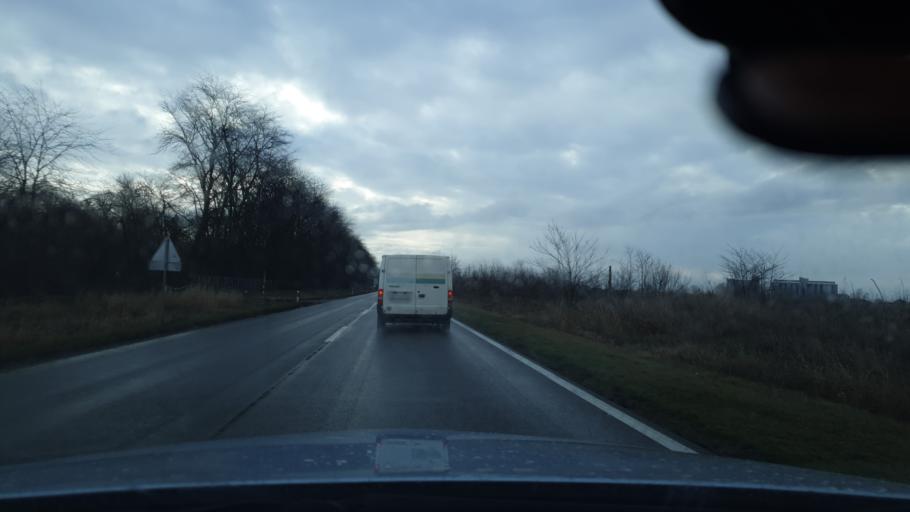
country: RS
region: Autonomna Pokrajina Vojvodina
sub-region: Juznobanatski Okrug
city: Kovin
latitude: 44.7597
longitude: 20.9597
